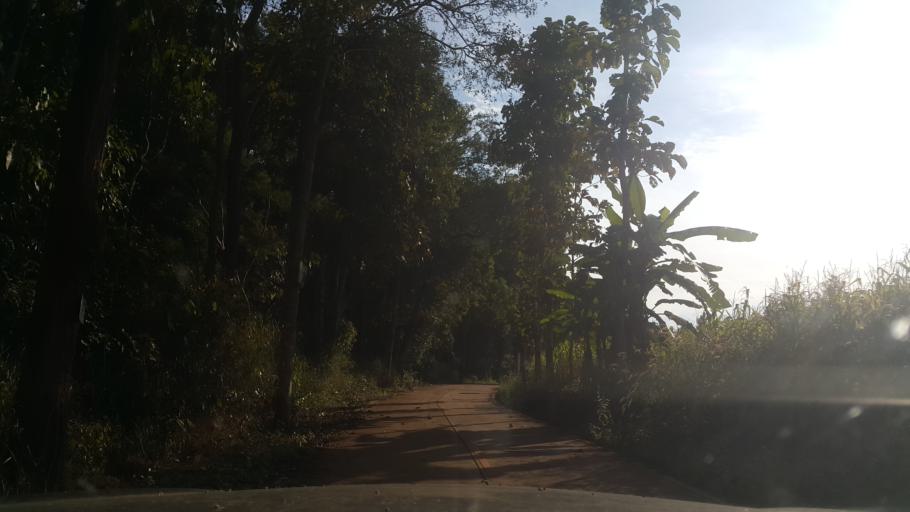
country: TH
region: Chiang Mai
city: Samoeng
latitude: 19.0018
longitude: 98.6849
